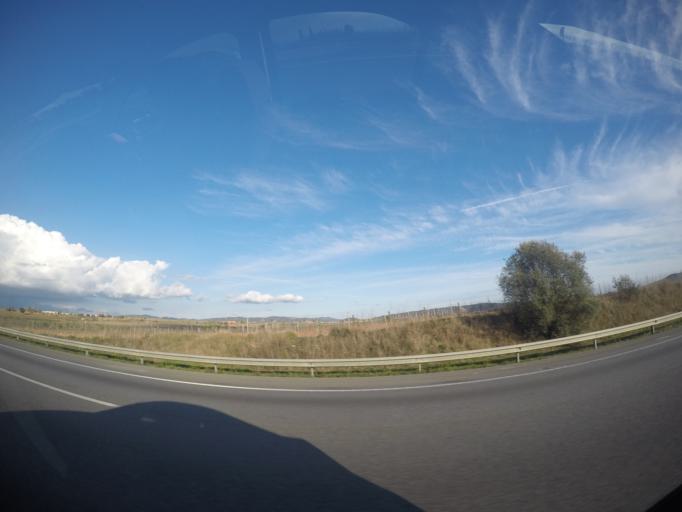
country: ES
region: Catalonia
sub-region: Provincia de Barcelona
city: La Granada
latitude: 41.3641
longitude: 1.7257
